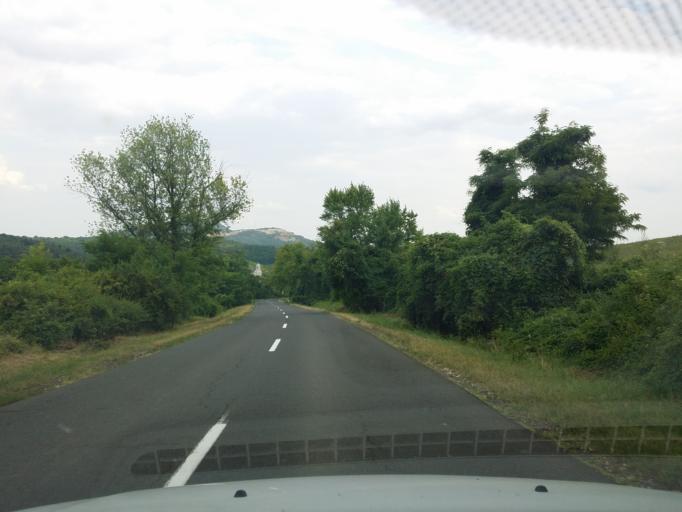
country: HU
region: Nograd
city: Bercel
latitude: 47.9167
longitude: 19.3697
